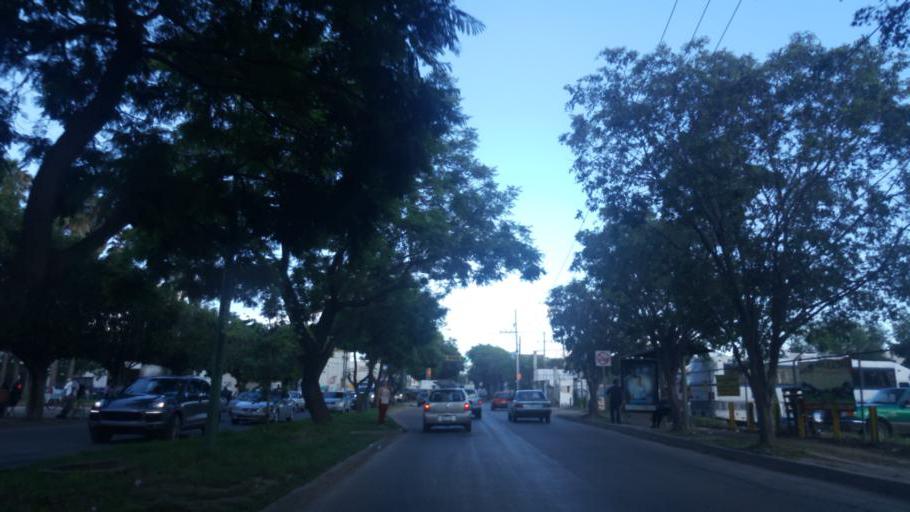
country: MX
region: Guanajuato
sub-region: Leon
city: San Jose de Duran (Los Troncoso)
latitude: 21.0933
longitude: -101.6873
